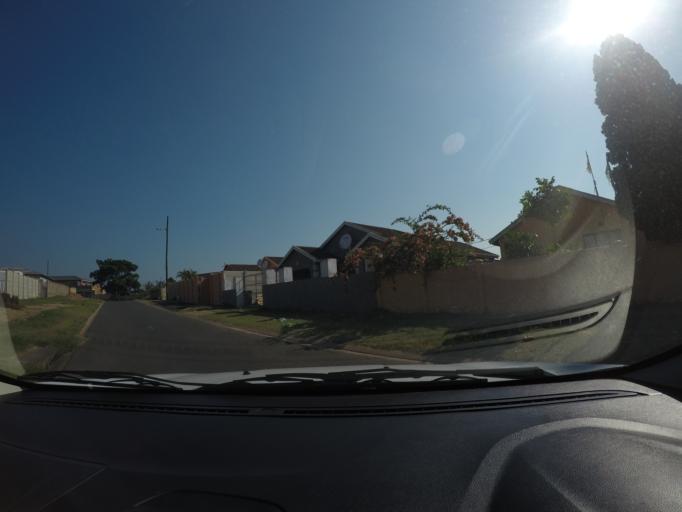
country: ZA
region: KwaZulu-Natal
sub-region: uThungulu District Municipality
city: Richards Bay
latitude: -28.7168
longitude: 32.0416
